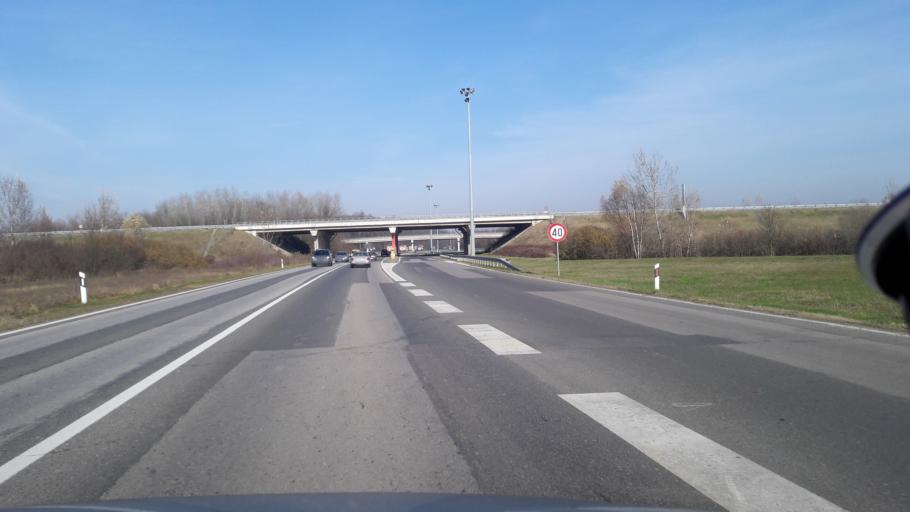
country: HR
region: Vukovarsko-Srijemska
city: Zupanja
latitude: 45.1044
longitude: 18.7009
